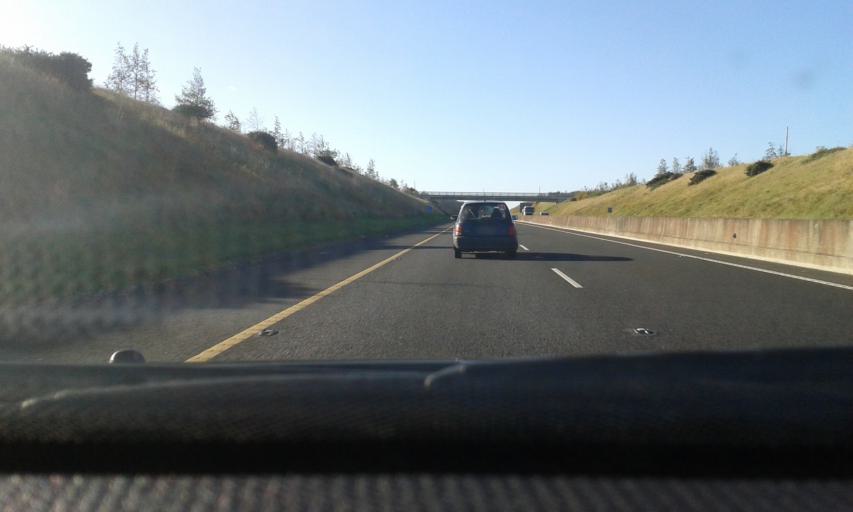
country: IE
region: Leinster
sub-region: Laois
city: Rathdowney
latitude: 52.7152
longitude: -7.6089
